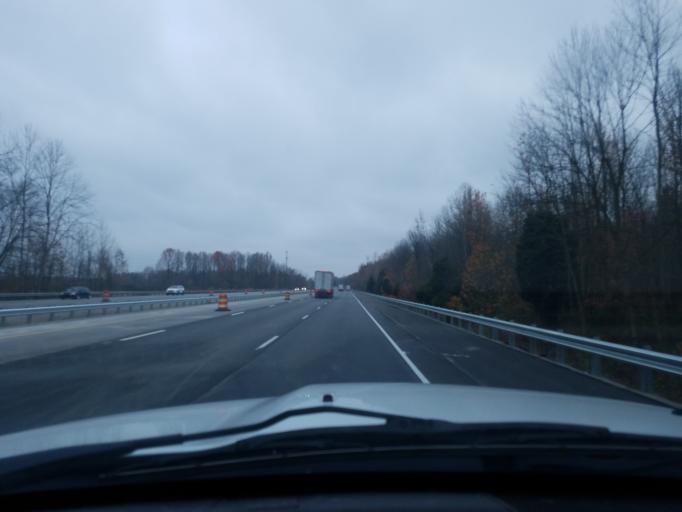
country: US
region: Indiana
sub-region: Clark County
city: Sellersburg
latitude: 38.4291
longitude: -85.7648
